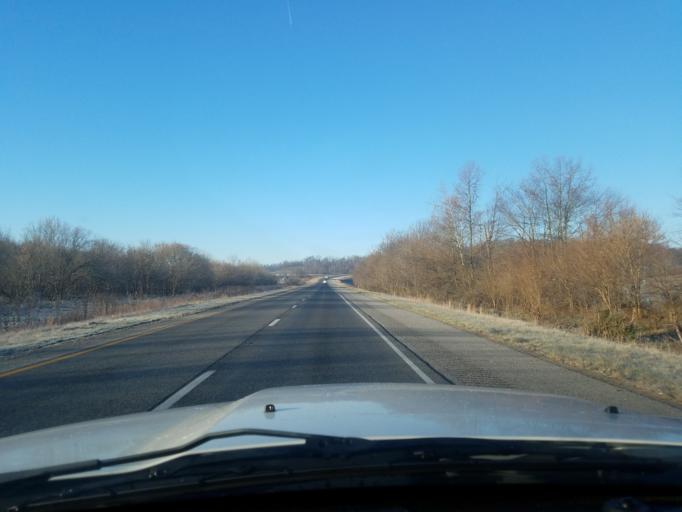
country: US
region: Indiana
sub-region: Dubois County
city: Ferdinand
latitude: 38.2092
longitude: -86.7780
